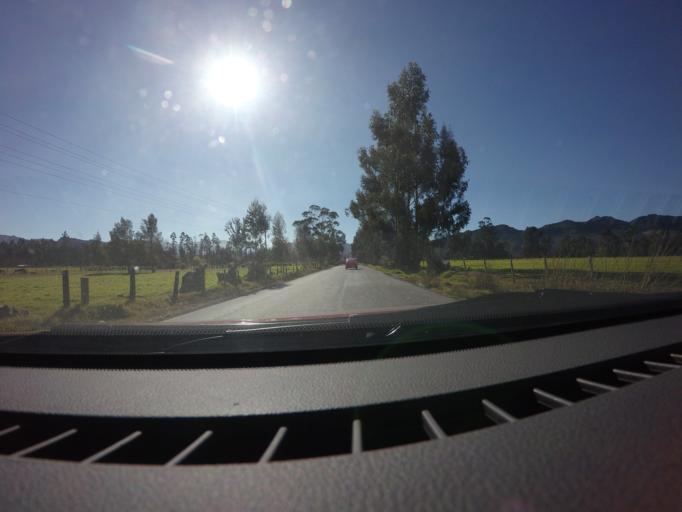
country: CO
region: Cundinamarca
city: Ubate
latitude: 5.2801
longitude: -73.8033
